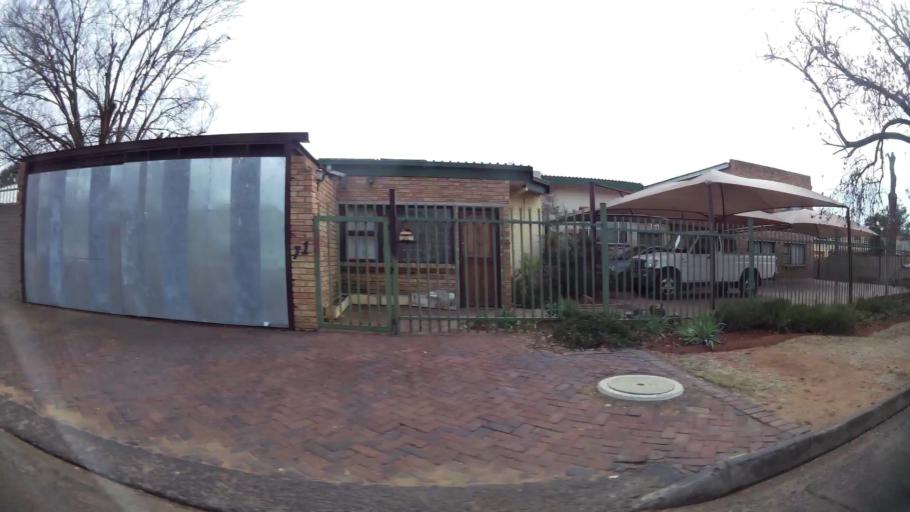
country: ZA
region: Orange Free State
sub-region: Mangaung Metropolitan Municipality
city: Bloemfontein
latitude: -29.1253
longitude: 26.1764
